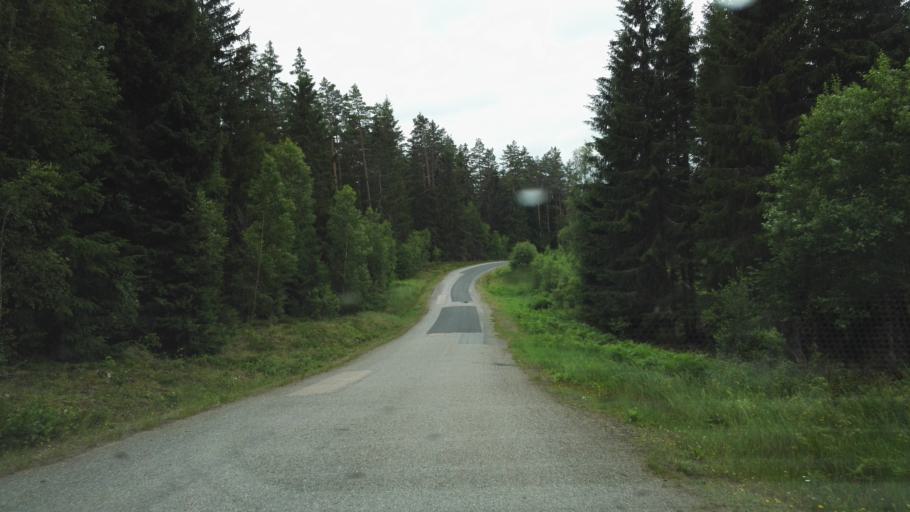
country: SE
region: Joenkoeping
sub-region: Vetlanda Kommun
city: Landsbro
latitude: 57.1998
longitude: 14.7915
